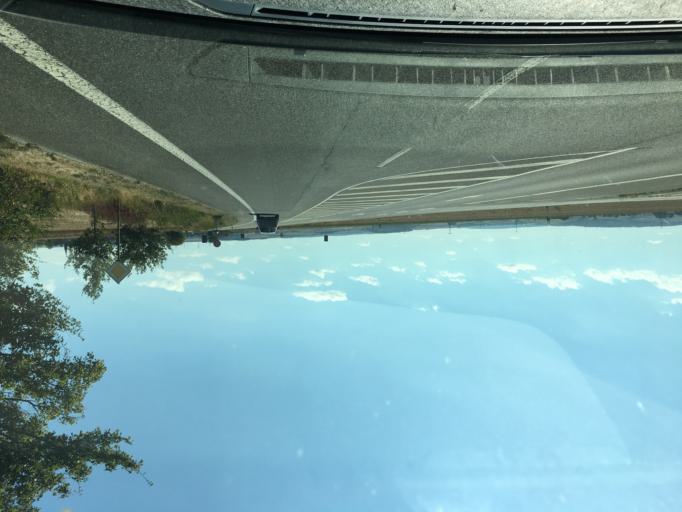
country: DE
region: North Rhine-Westphalia
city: Zulpich
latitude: 50.6829
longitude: 6.6336
